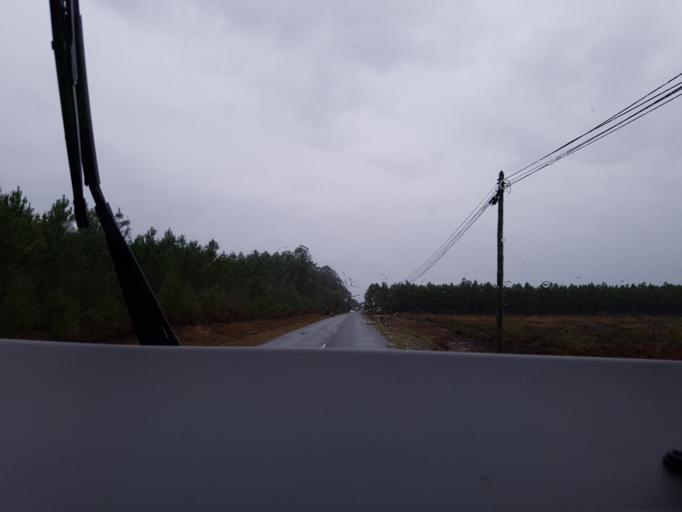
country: FR
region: Aquitaine
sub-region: Departement de la Gironde
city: Saint-Symphorien
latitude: 44.3479
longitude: -0.6162
